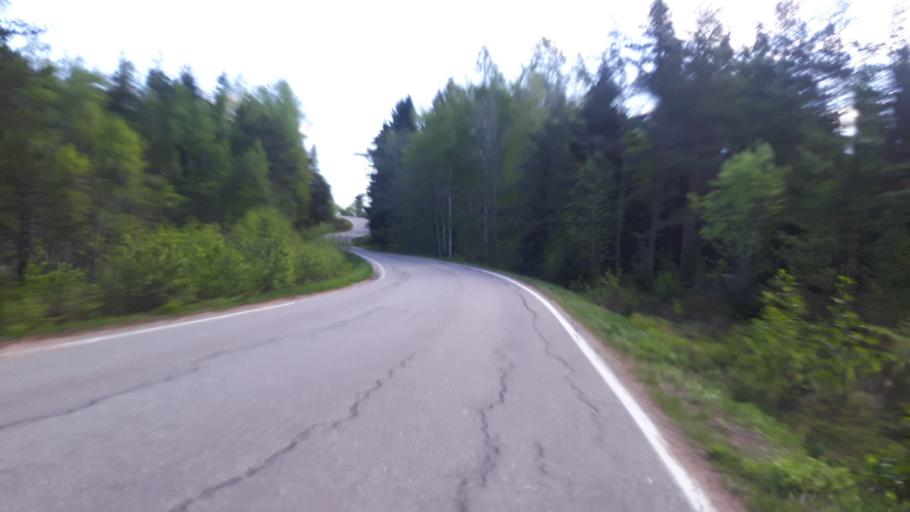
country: FI
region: Kymenlaakso
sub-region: Kotka-Hamina
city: Hamina
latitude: 60.5138
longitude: 27.4120
